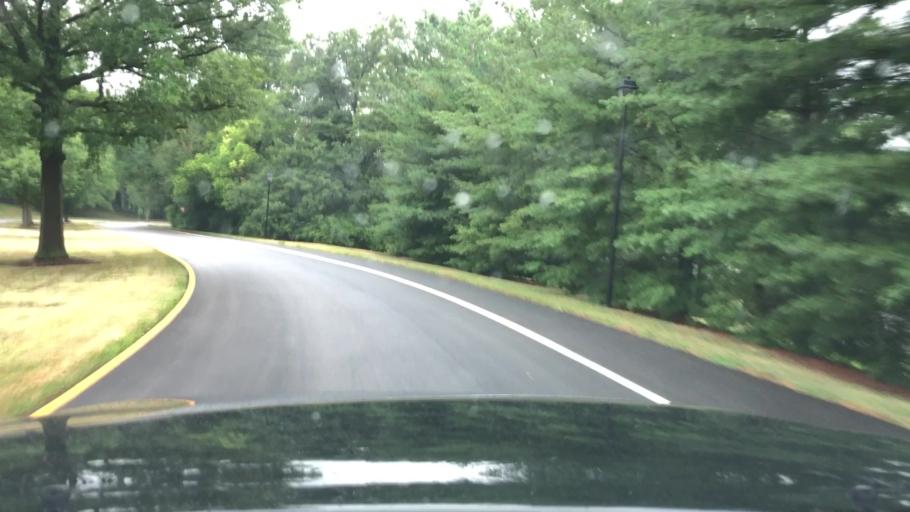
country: US
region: Missouri
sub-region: Saint Charles County
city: Lake Saint Louis
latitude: 38.8020
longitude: -90.7920
